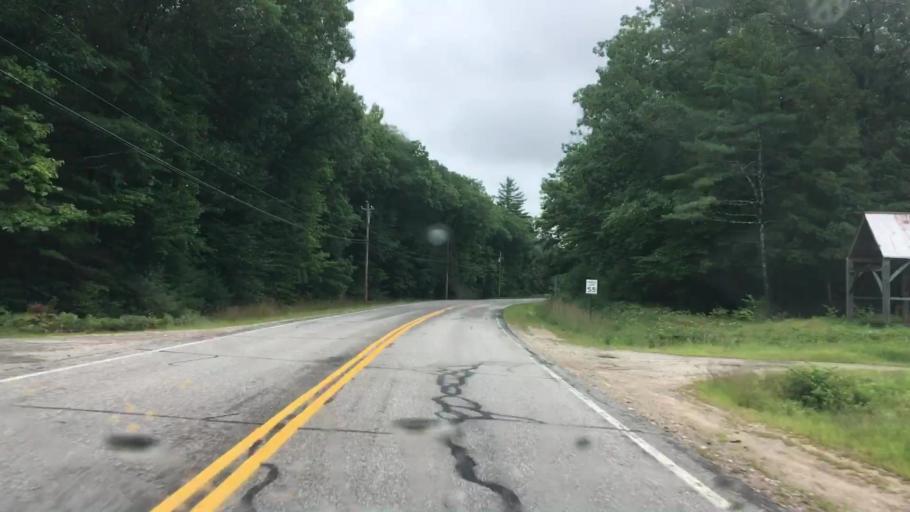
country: US
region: Maine
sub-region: Oxford County
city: Fryeburg
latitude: 44.0094
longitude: -70.9564
